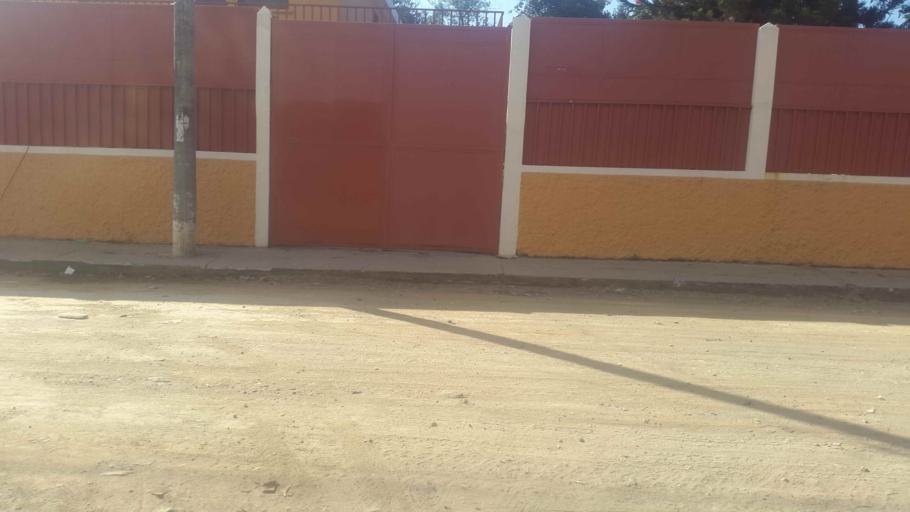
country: GT
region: Guatemala
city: Petapa
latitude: 14.5139
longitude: -90.5428
